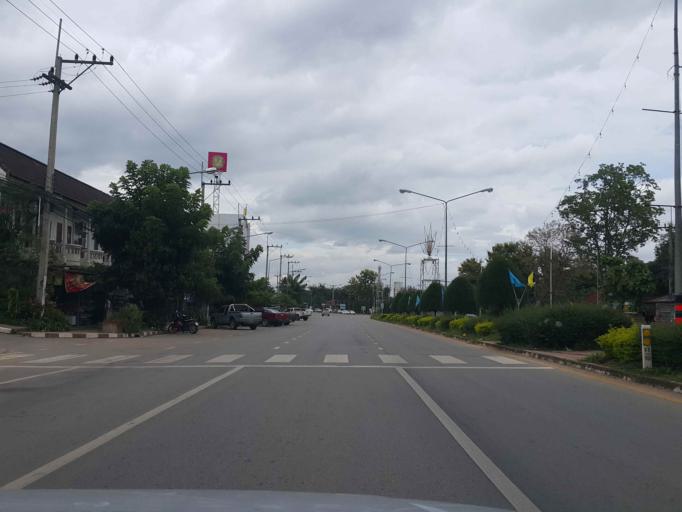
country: TH
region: Lamphun
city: Li
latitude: 17.8006
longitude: 98.9500
